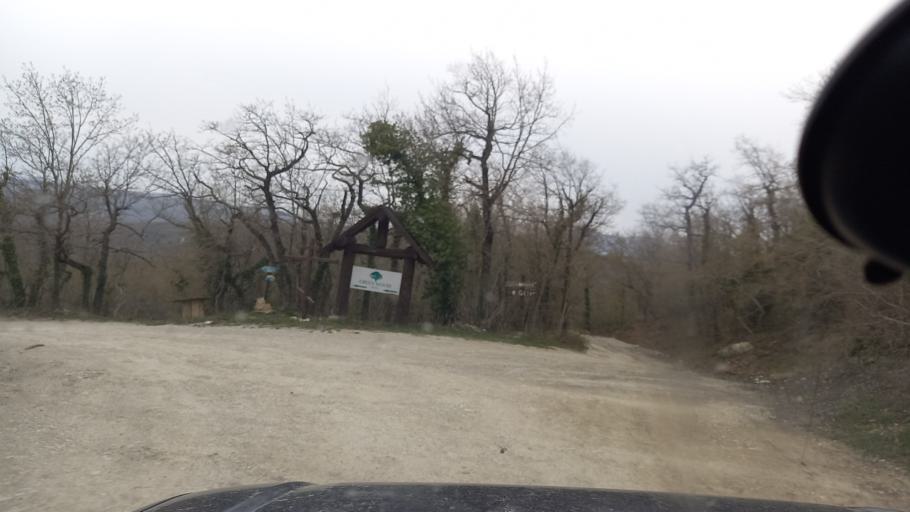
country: RU
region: Krasnodarskiy
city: Dzhubga
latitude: 44.3199
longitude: 38.6770
